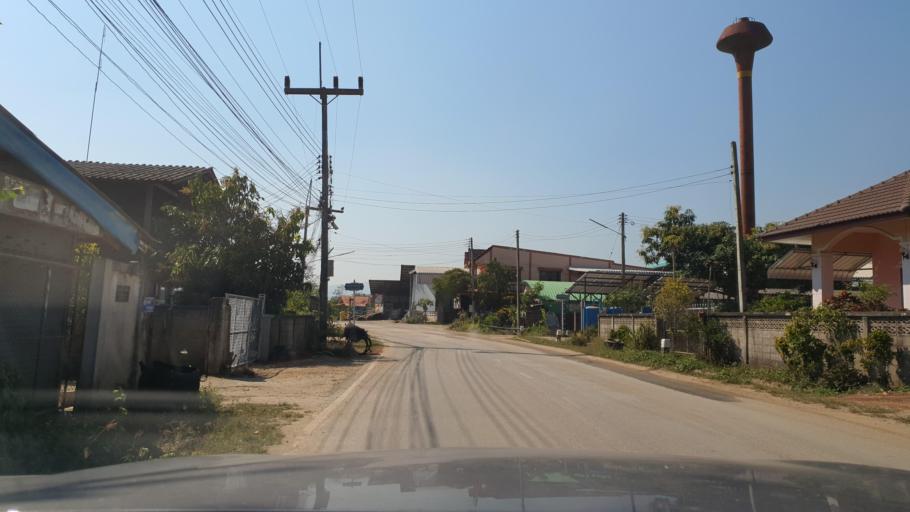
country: TH
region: Chiang Rai
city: Mae Lao
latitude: 19.7646
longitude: 99.7274
